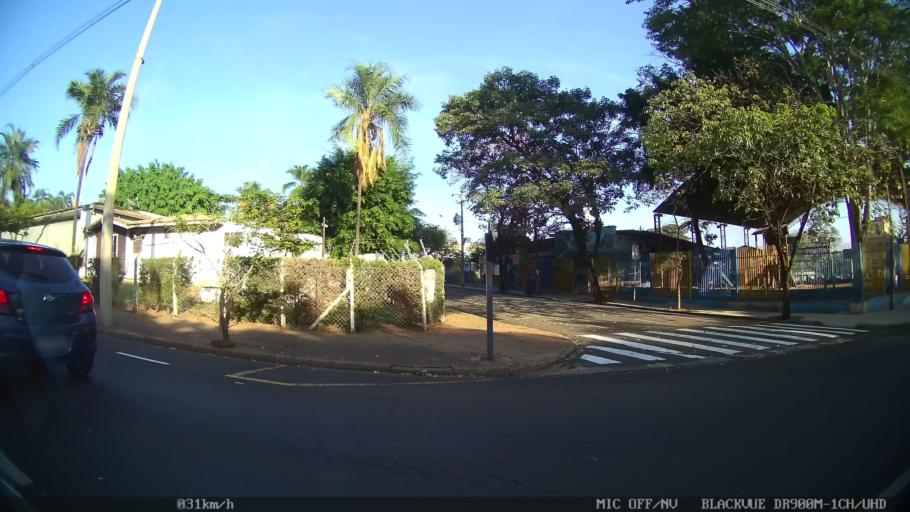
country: BR
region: Sao Paulo
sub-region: Sao Jose Do Rio Preto
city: Sao Jose do Rio Preto
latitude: -20.8224
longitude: -49.3661
